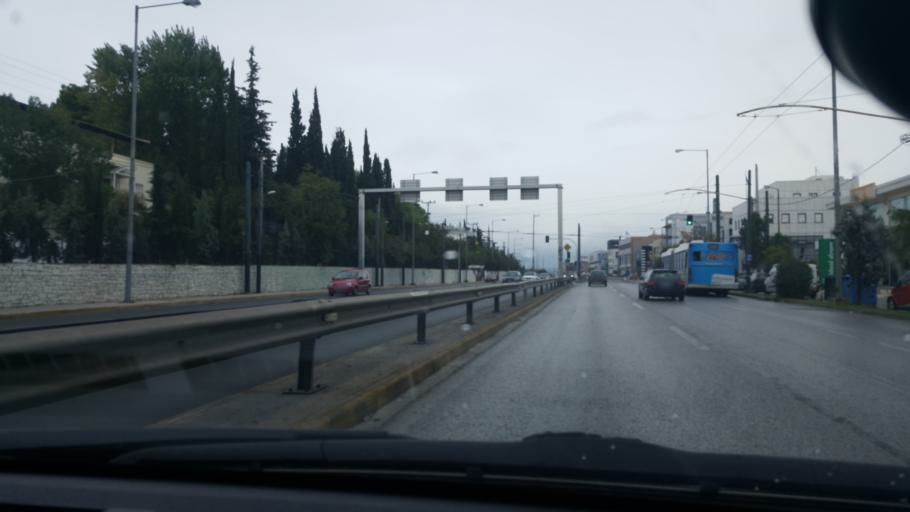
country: GR
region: Attica
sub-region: Nomarchia Athinas
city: Psychiko
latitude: 38.0016
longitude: 23.7729
